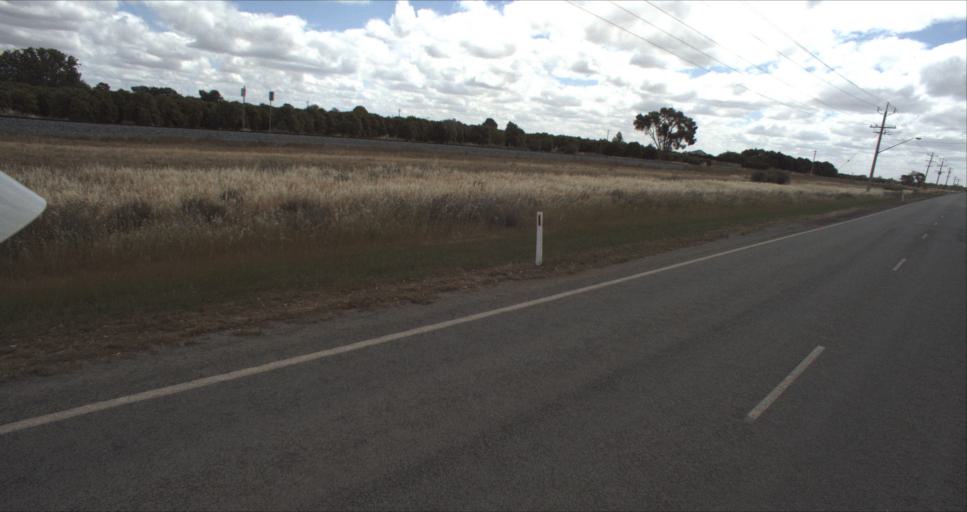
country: AU
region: New South Wales
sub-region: Leeton
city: Leeton
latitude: -34.5806
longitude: 146.4001
